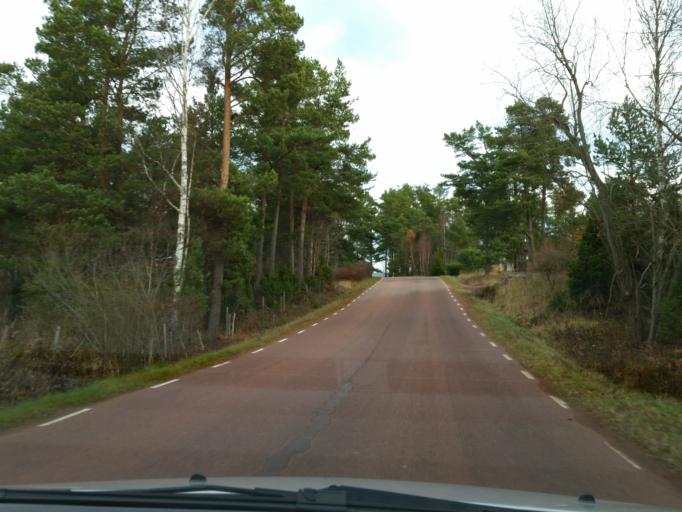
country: AX
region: Alands landsbygd
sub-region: Finstroem
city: Finstroem
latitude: 60.2368
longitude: 19.9741
